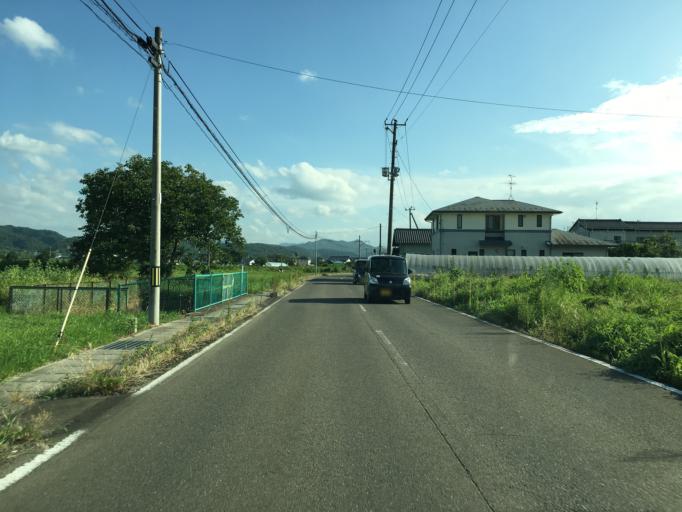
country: JP
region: Fukushima
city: Yanagawamachi-saiwaicho
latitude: 37.8309
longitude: 140.5831
